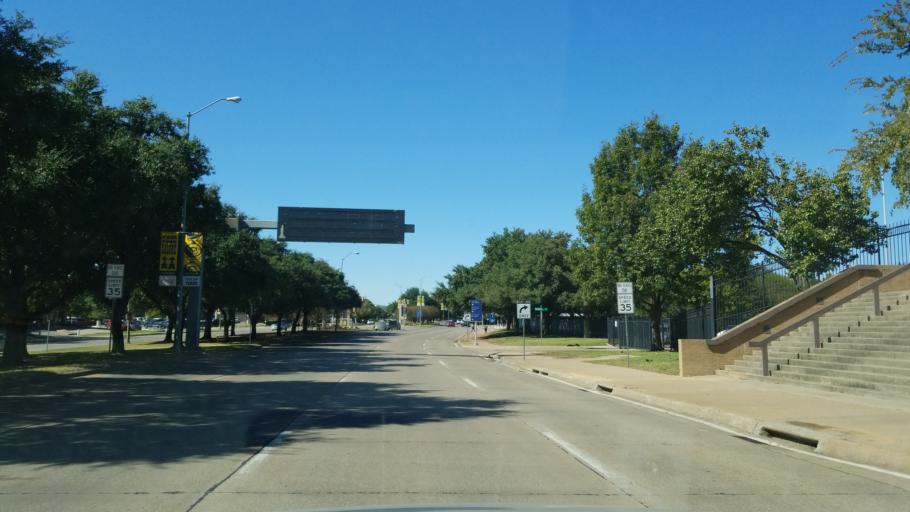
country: US
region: Texas
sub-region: Dallas County
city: Dallas
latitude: 32.7737
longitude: -96.7608
